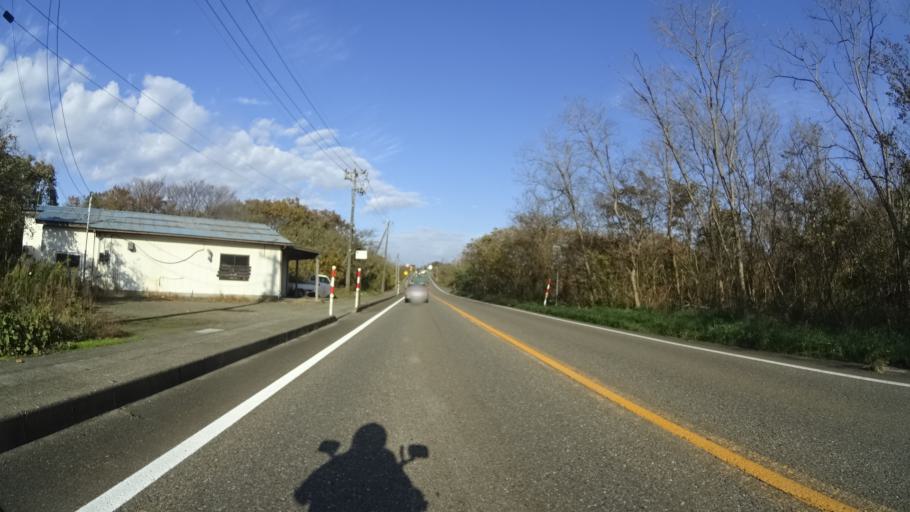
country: JP
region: Niigata
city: Joetsu
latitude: 37.2609
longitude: 138.3709
